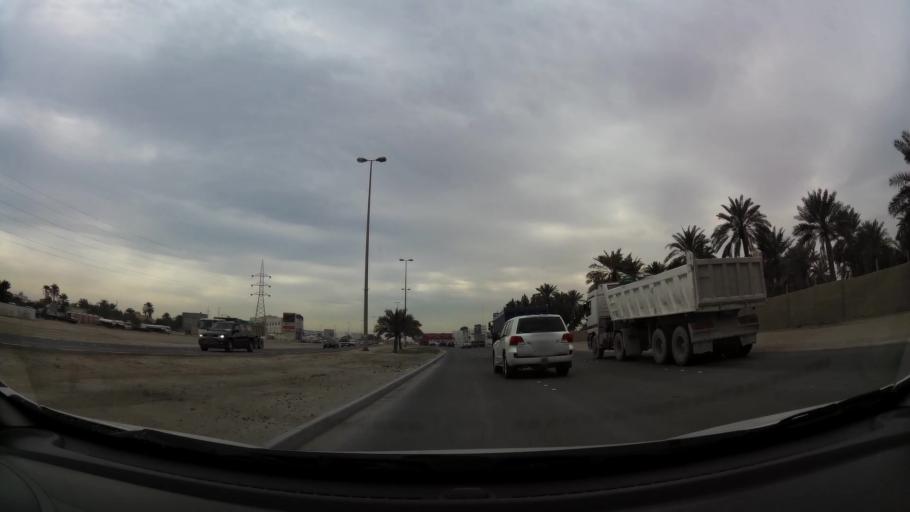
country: BH
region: Northern
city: Sitrah
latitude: 26.1613
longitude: 50.6046
